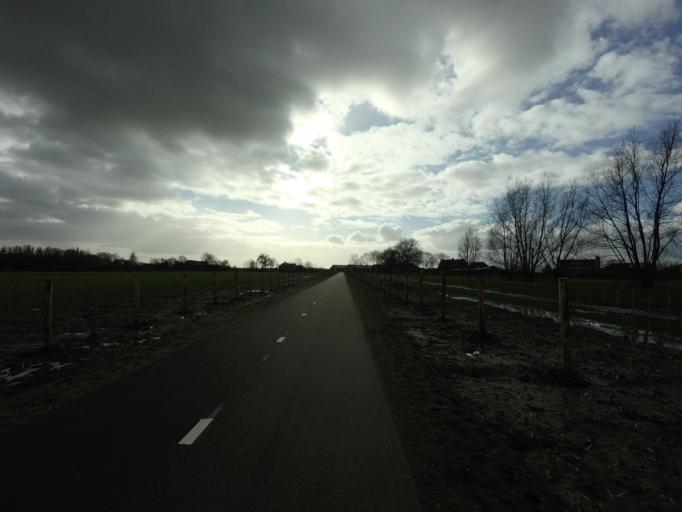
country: NL
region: Utrecht
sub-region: Gemeente IJsselstein
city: IJsselstein
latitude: 52.0490
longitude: 5.0221
